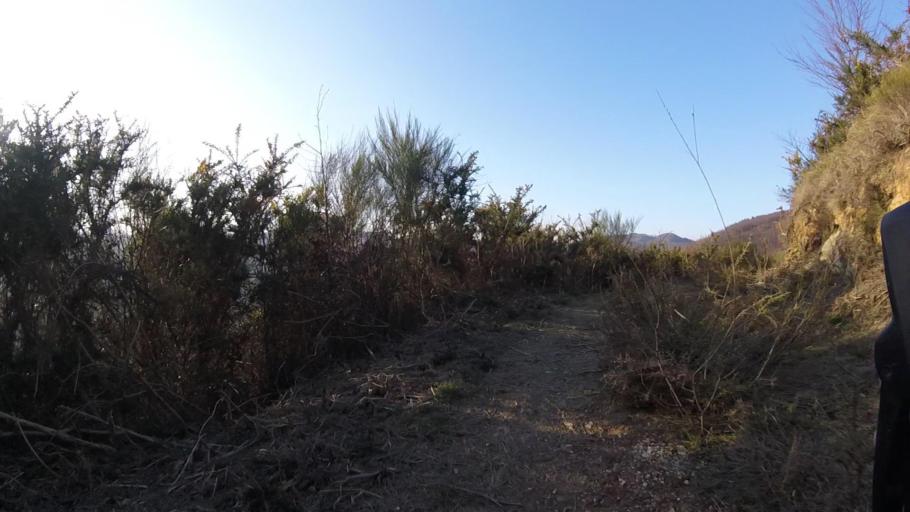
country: ES
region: Navarre
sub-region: Provincia de Navarra
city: Arano
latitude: 43.2276
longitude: -1.8626
